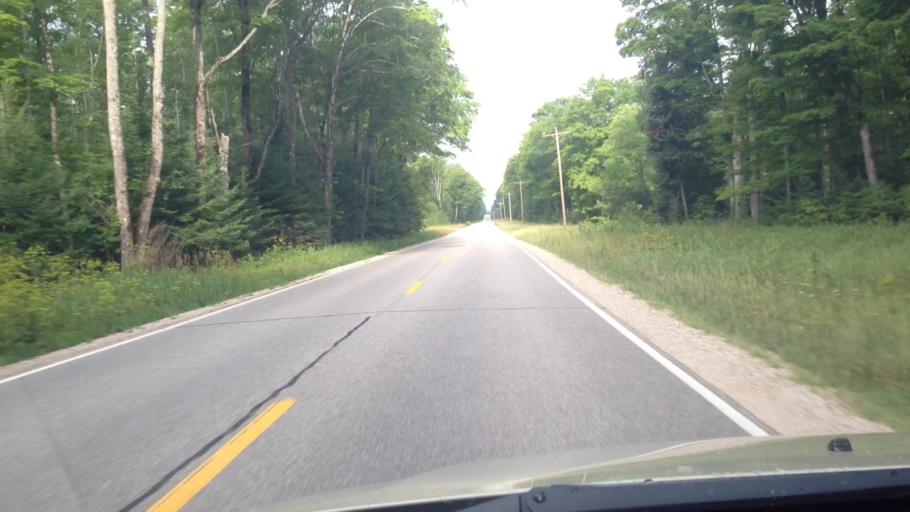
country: US
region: Michigan
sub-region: Mackinac County
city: Saint Ignace
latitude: 46.0570
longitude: -85.1267
